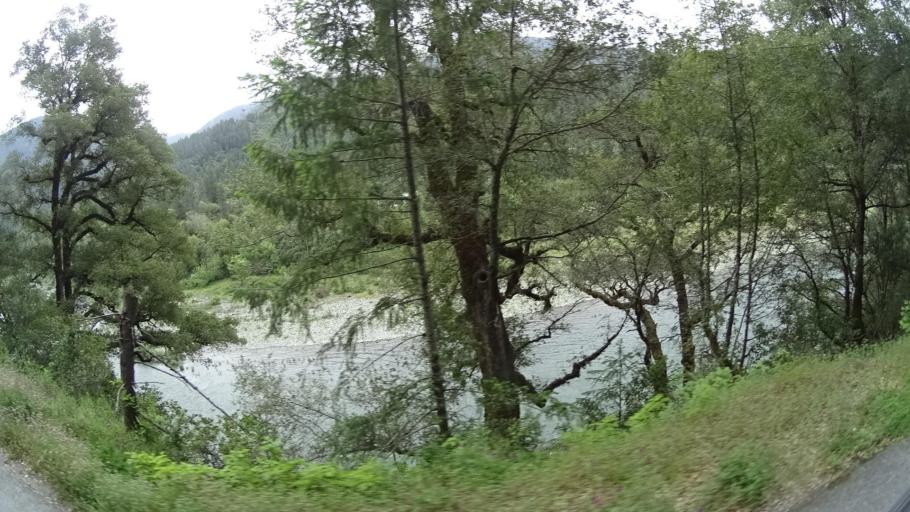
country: US
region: California
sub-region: Humboldt County
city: Willow Creek
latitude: 41.3066
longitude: -123.5334
